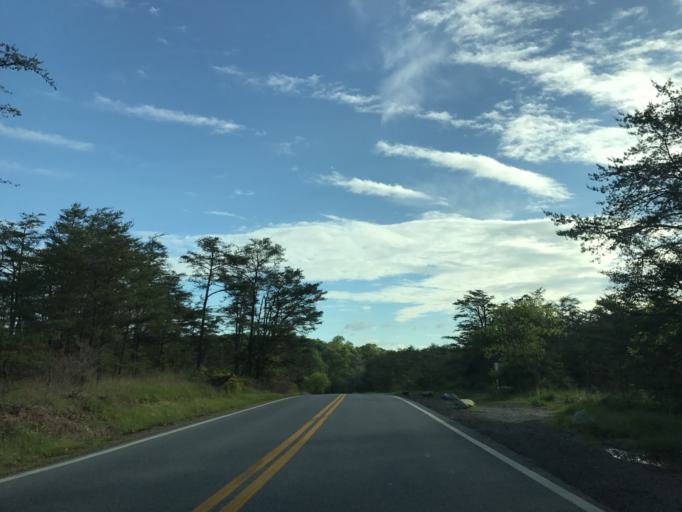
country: US
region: Maryland
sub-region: Baltimore County
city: Randallstown
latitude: 39.4012
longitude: -76.8240
